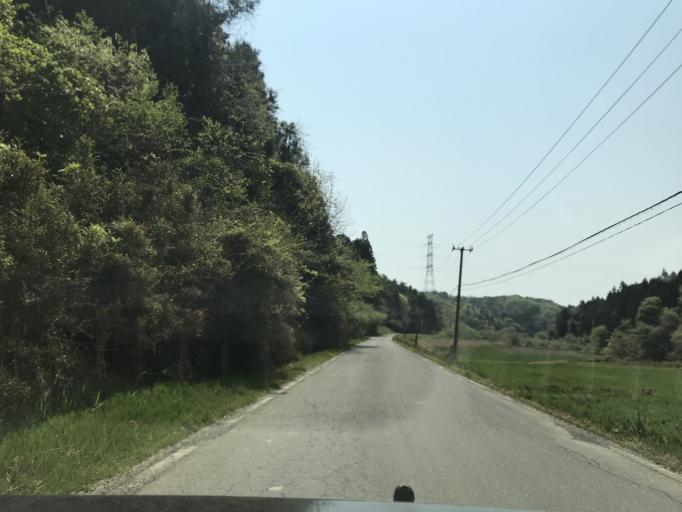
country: JP
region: Iwate
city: Ichinoseki
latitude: 38.8461
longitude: 141.0682
